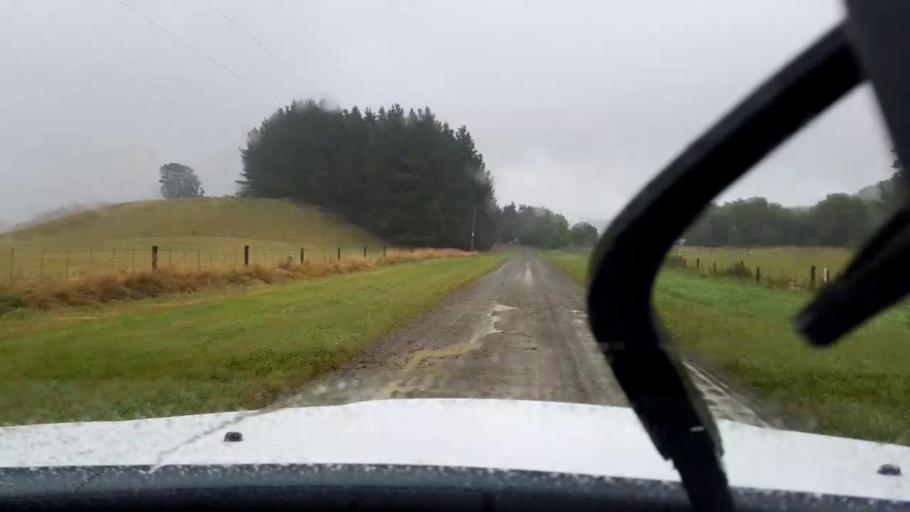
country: NZ
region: Canterbury
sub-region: Timaru District
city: Pleasant Point
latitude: -44.1659
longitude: 171.1761
